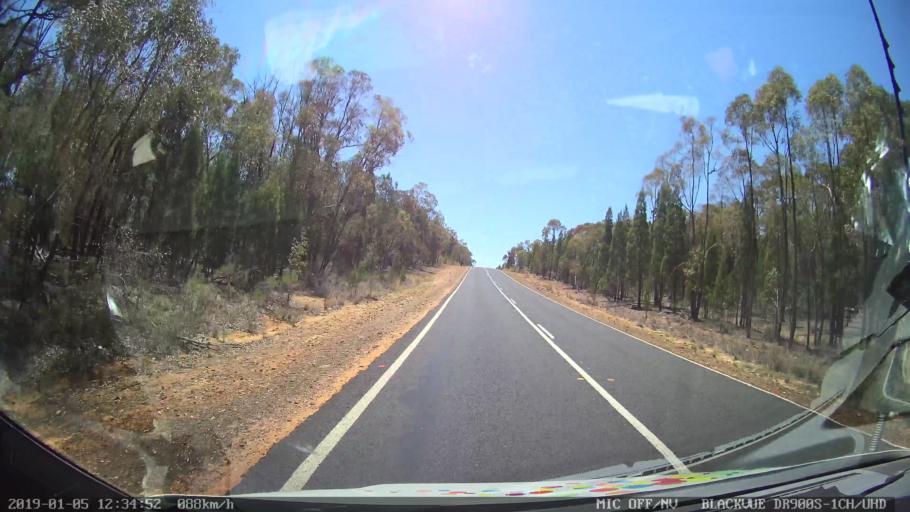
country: AU
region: New South Wales
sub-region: Warrumbungle Shire
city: Coonabarabran
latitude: -31.2110
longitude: 149.4169
